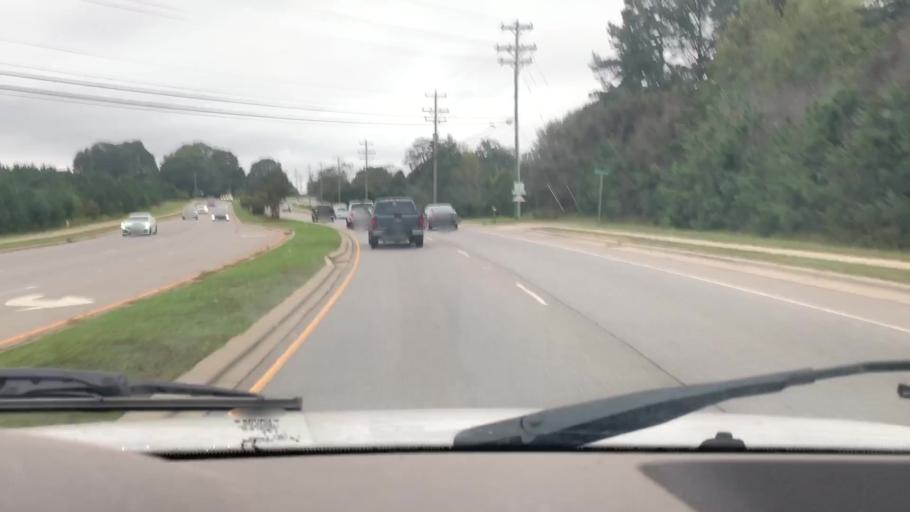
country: US
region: North Carolina
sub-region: Catawba County
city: Lake Norman of Catawba
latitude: 35.5724
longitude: -80.8959
